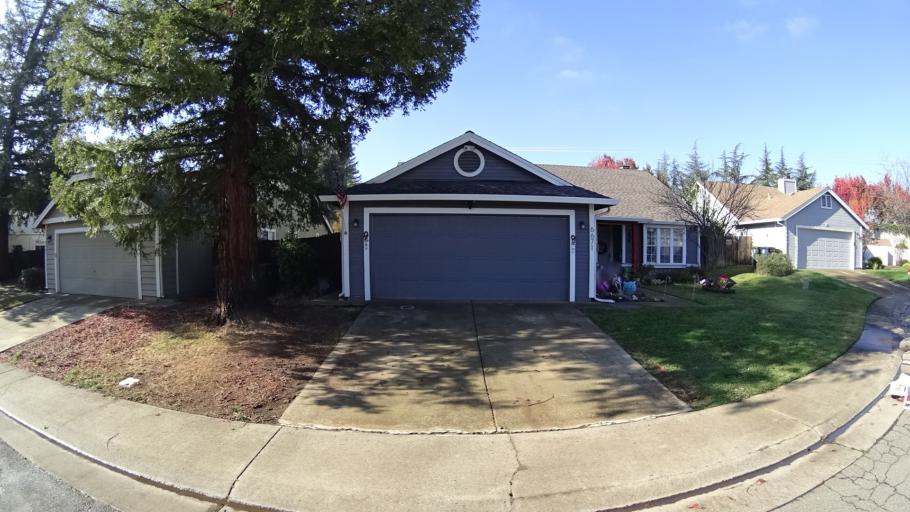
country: US
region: California
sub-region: Sacramento County
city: Antelope
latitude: 38.6880
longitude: -121.3289
